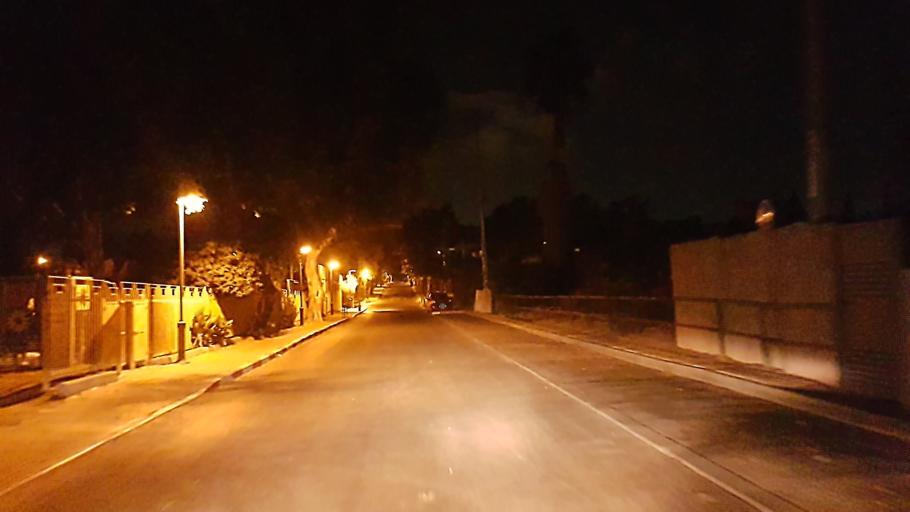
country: IL
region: Central District
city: Hod HaSharon
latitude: 32.1649
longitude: 34.8866
